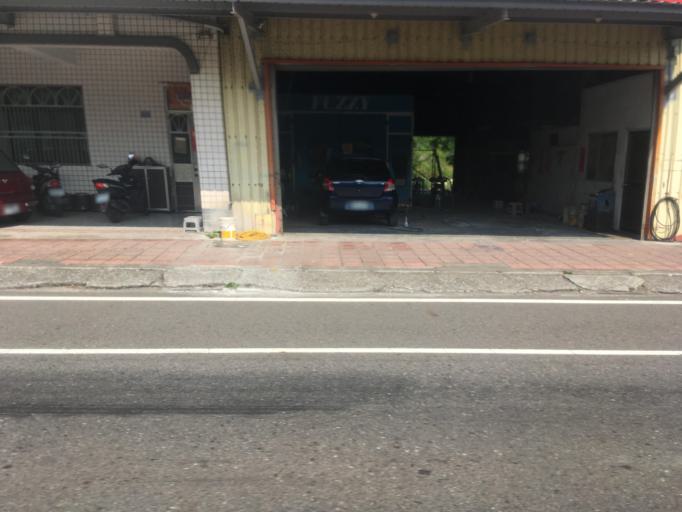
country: TW
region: Taiwan
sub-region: Yilan
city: Yilan
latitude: 24.6385
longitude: 121.8337
